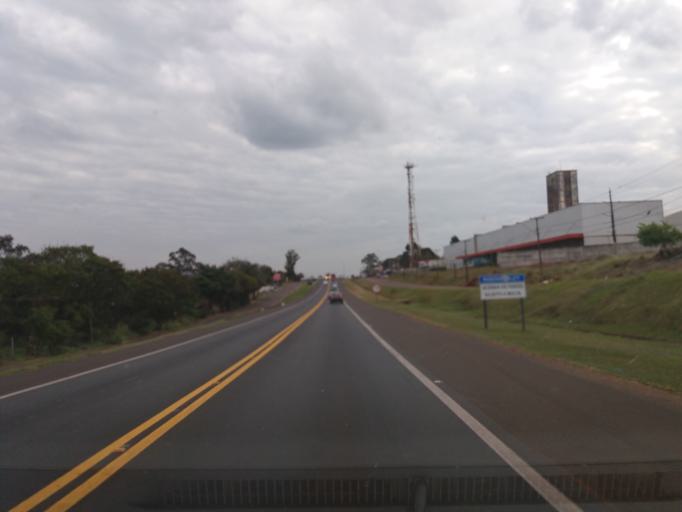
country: BR
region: Parana
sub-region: Cascavel
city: Cascavel
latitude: -24.9824
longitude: -53.4589
